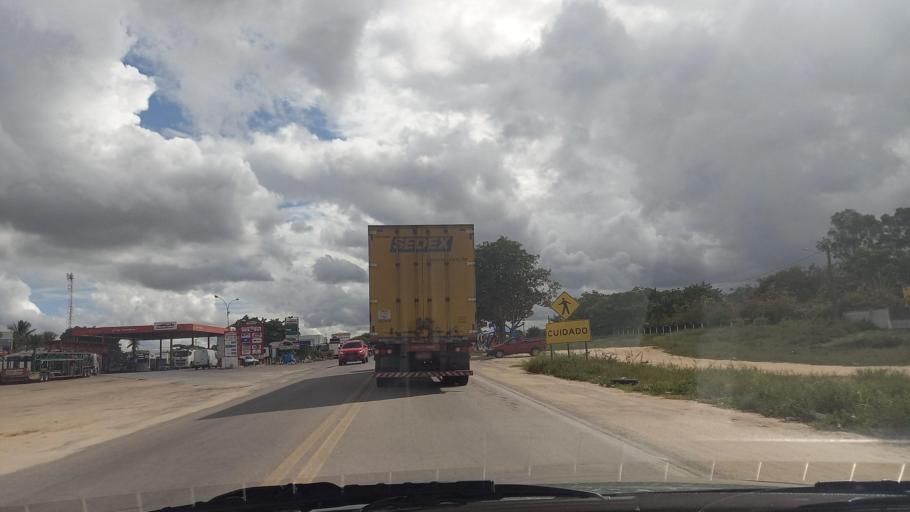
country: BR
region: Pernambuco
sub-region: Lajedo
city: Lajedo
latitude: -8.6577
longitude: -36.3288
